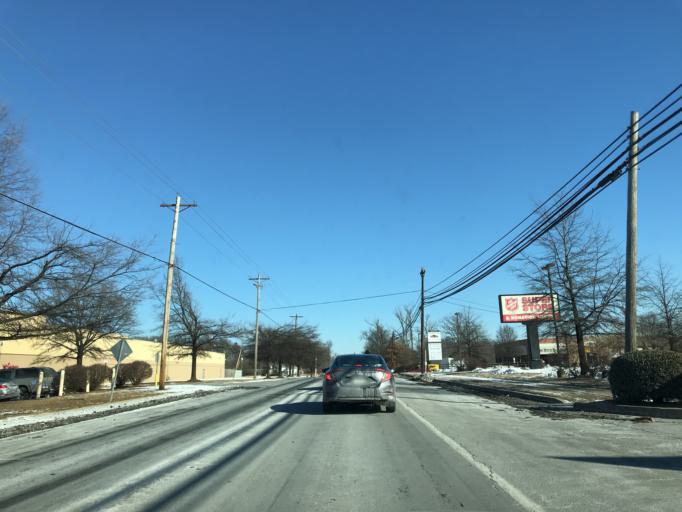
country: US
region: Maryland
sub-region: Charles County
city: Waldorf
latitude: 38.6378
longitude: -76.8950
